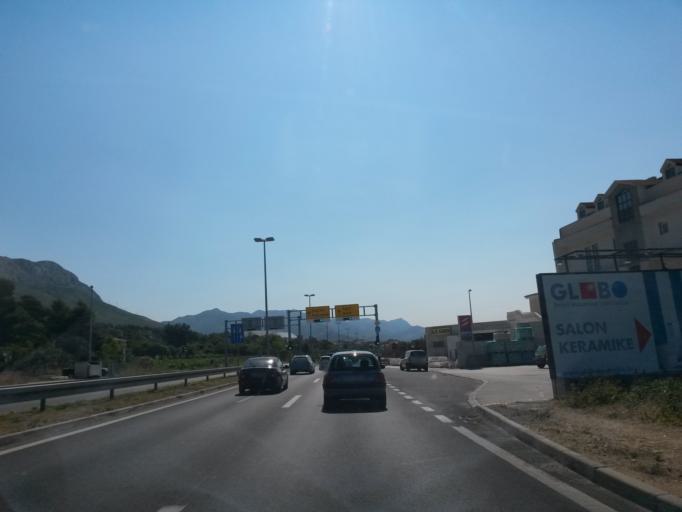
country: HR
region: Splitsko-Dalmatinska
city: Vranjic
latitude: 43.5507
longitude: 16.4329
